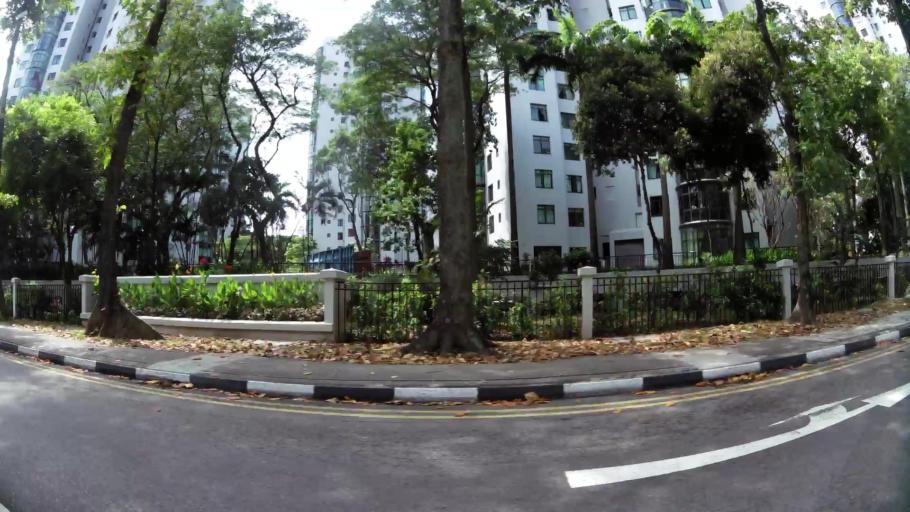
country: MY
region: Johor
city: Johor Bahru
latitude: 1.3443
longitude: 103.7344
